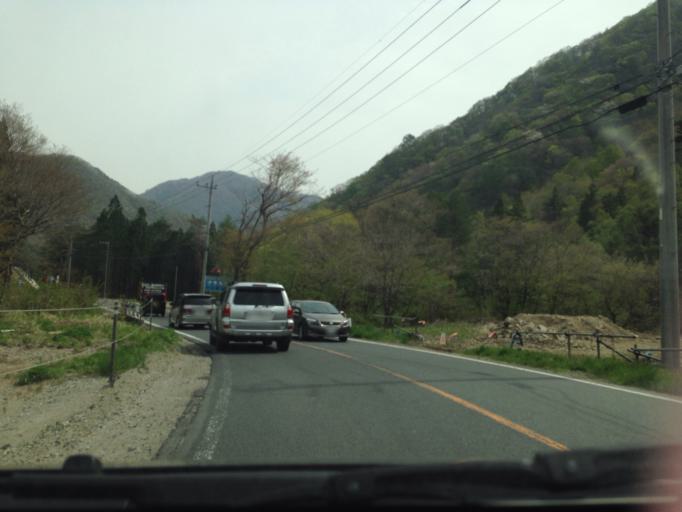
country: JP
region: Tochigi
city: Nikko
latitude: 37.0238
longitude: 139.7270
